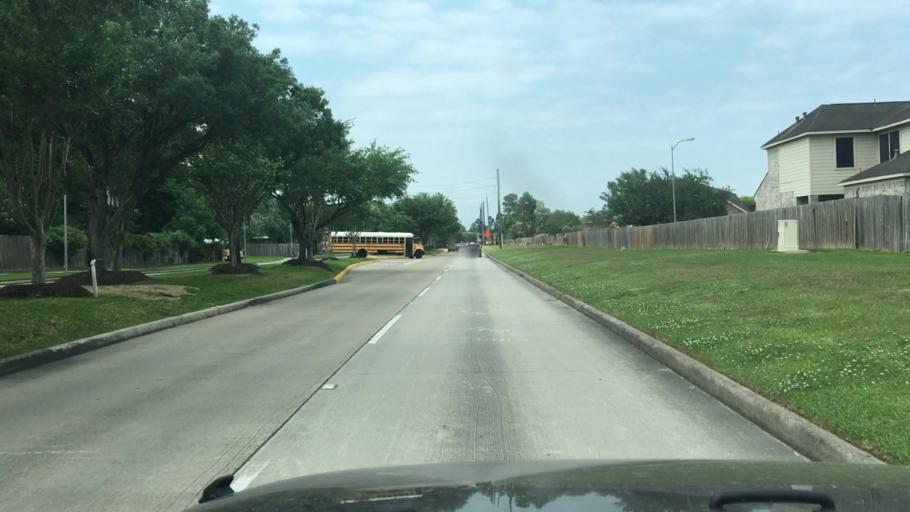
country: US
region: Texas
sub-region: Harris County
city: Atascocita
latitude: 29.9695
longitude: -95.2112
